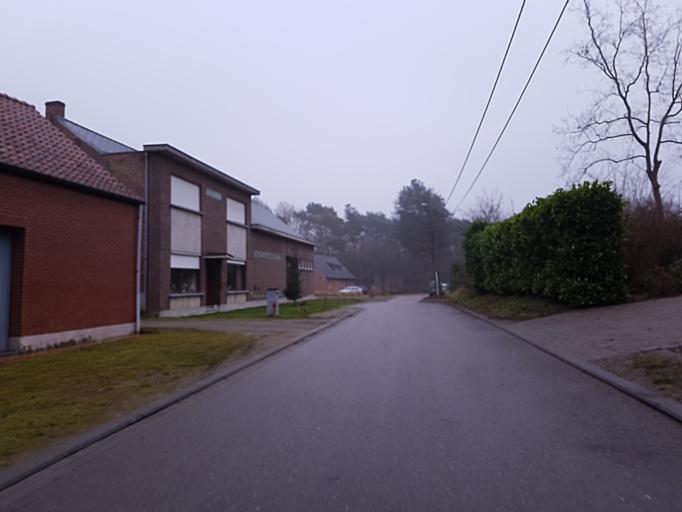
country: BE
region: Flanders
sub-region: Provincie Vlaams-Brabant
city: Keerbergen
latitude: 50.9961
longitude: 4.6073
